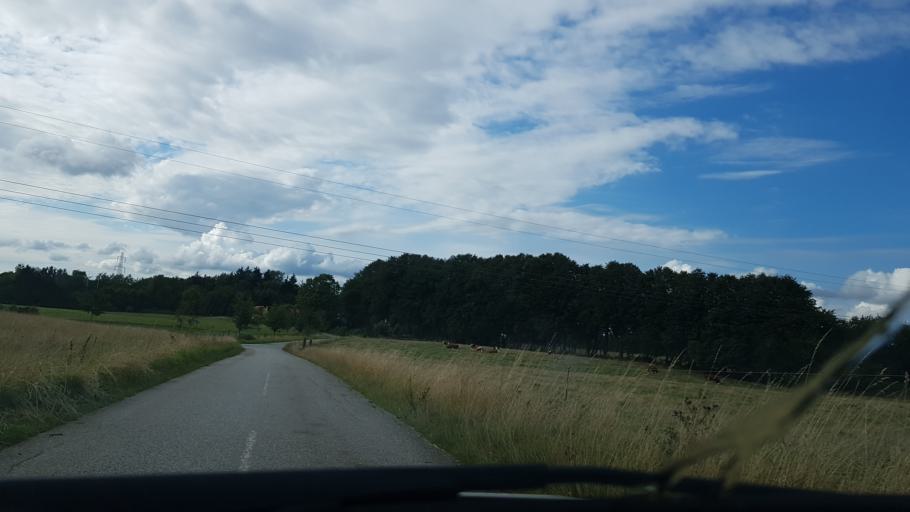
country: DK
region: Capital Region
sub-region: Fredensborg Kommune
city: Niva
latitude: 55.9811
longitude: 12.4849
